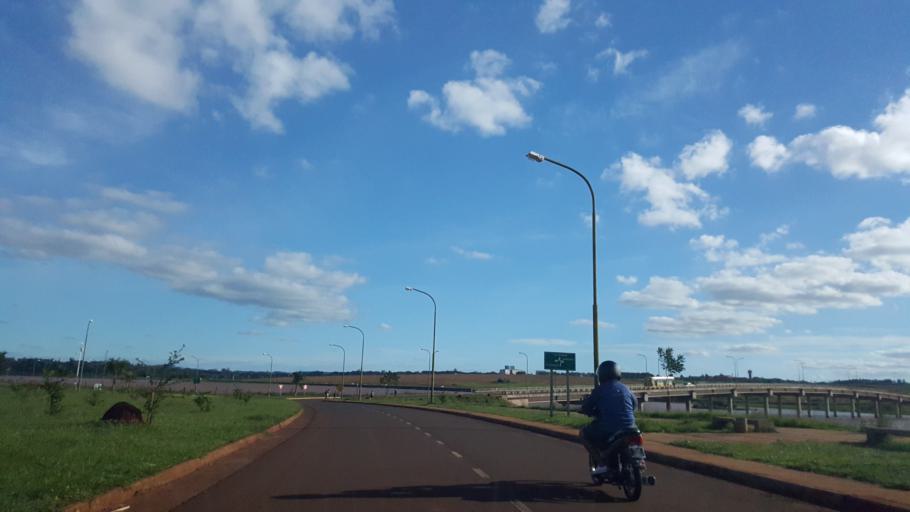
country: AR
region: Misiones
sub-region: Departamento de Capital
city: Posadas
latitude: -27.3808
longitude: -55.9527
